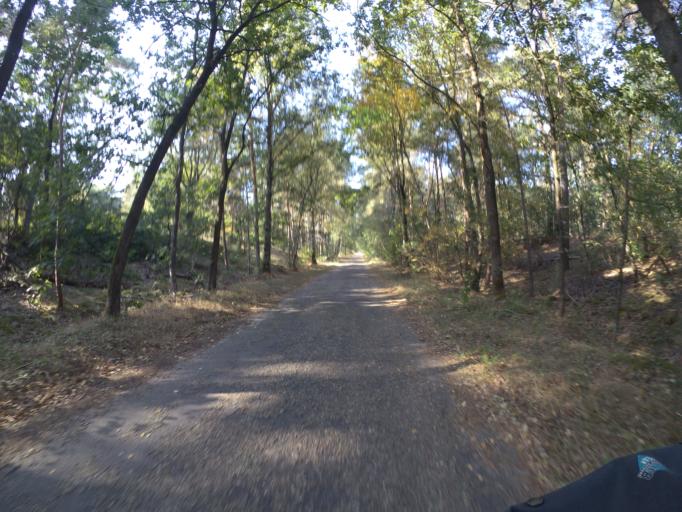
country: NL
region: North Brabant
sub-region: Gemeente Oirschot
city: Oirschot
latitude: 51.4707
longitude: 5.3320
